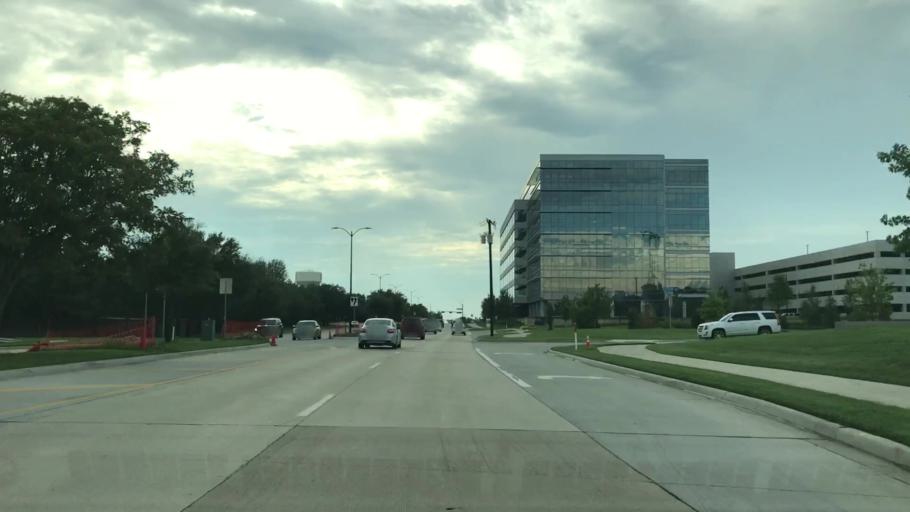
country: US
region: Texas
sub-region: Collin County
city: Frisco
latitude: 33.1068
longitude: -96.8307
